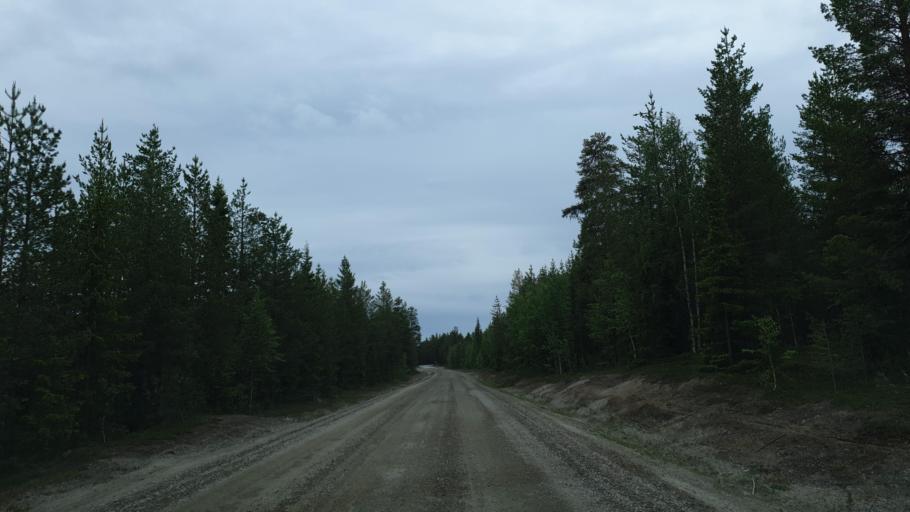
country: SE
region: Vaesterbotten
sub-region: Sorsele Kommun
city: Sorsele
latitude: 65.5551
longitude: 17.5057
